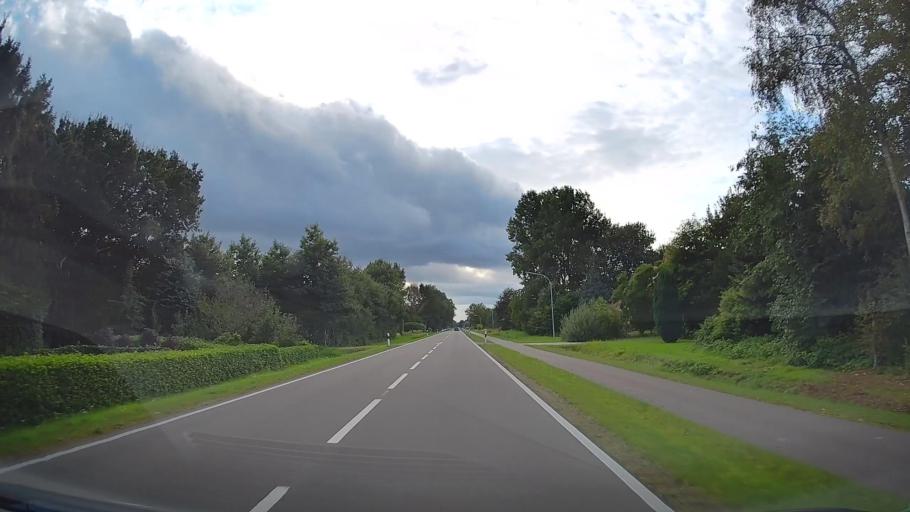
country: DE
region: Lower Saxony
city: Friesoythe
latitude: 53.0536
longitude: 7.7714
